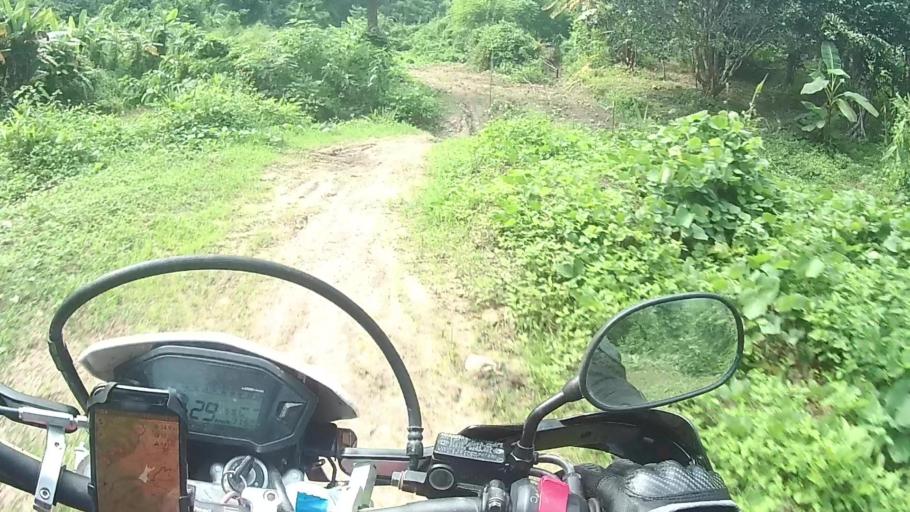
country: TH
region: Chiang Mai
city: Mae Taeng
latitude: 19.0114
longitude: 98.8494
